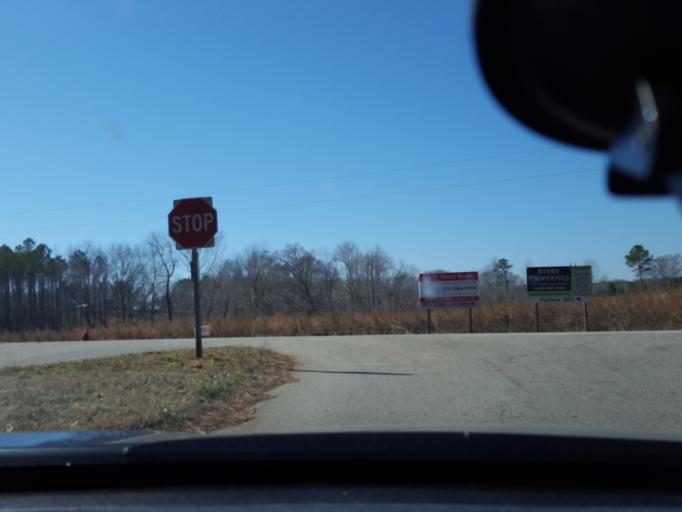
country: US
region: North Carolina
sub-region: Halifax County
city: South Rosemary
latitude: 36.4573
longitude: -77.9193
